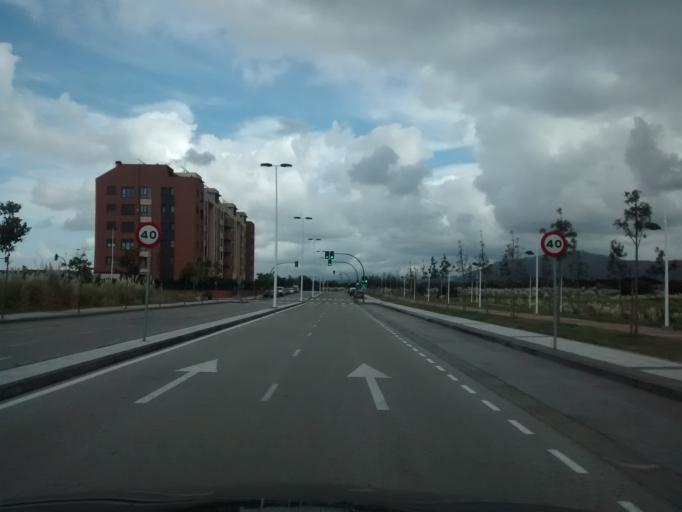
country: ES
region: Cantabria
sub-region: Provincia de Cantabria
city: Camargo
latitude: 43.4386
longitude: -3.8547
